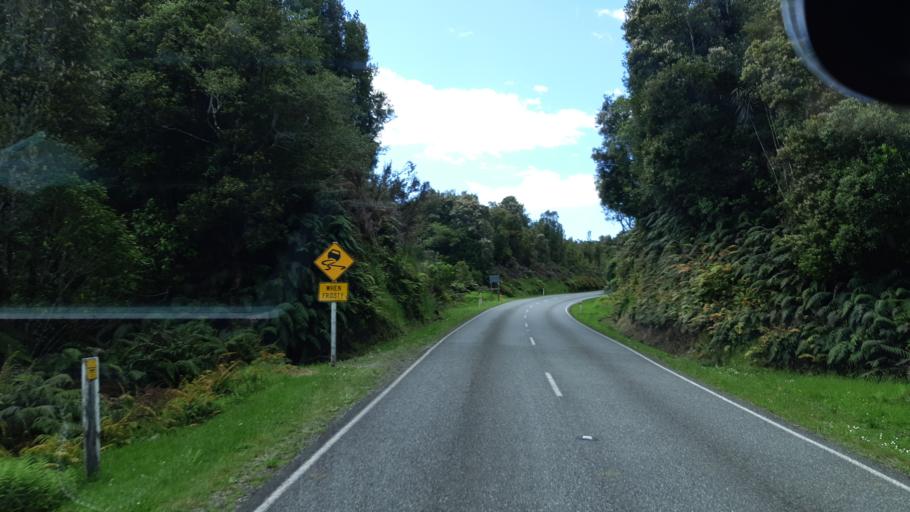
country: NZ
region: West Coast
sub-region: Westland District
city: Hokitika
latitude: -43.0482
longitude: 170.6379
